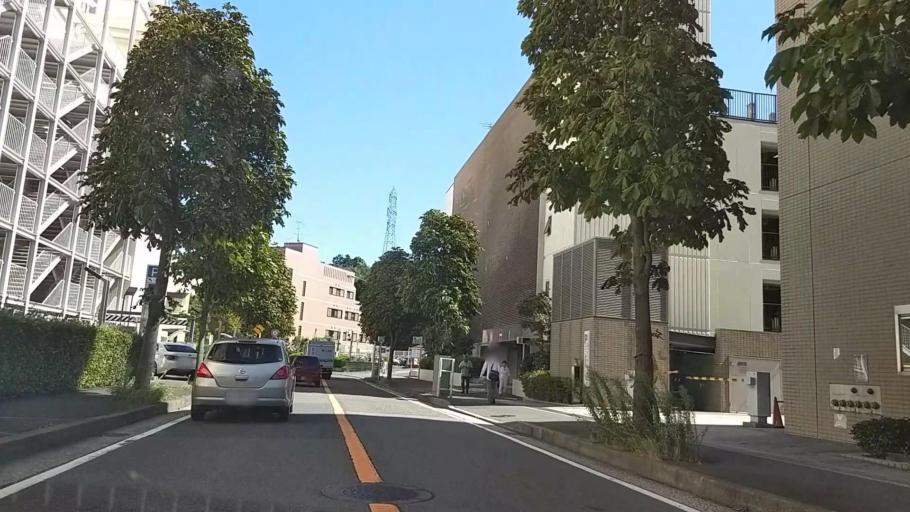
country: JP
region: Tokyo
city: Chofugaoka
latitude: 35.6025
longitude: 139.5094
